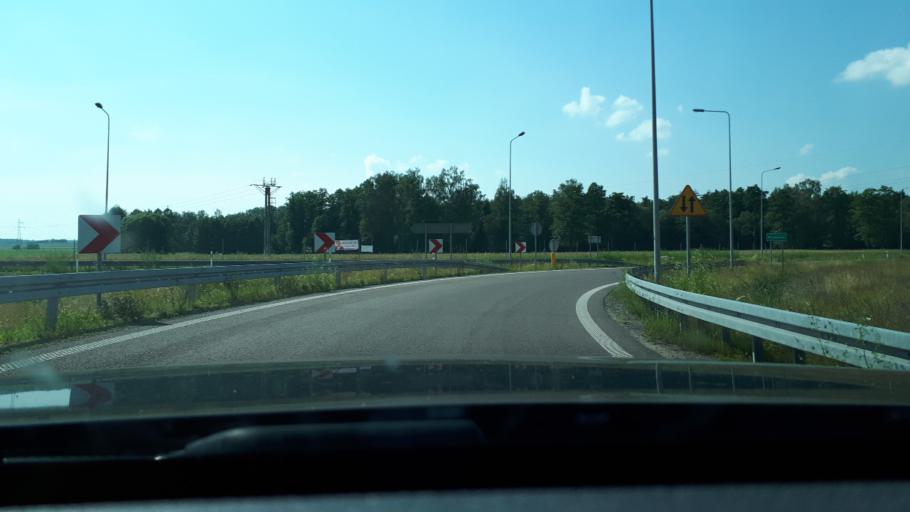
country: PL
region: Podlasie
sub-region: Powiat bialostocki
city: Tykocin
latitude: 53.1552
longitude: 22.8645
